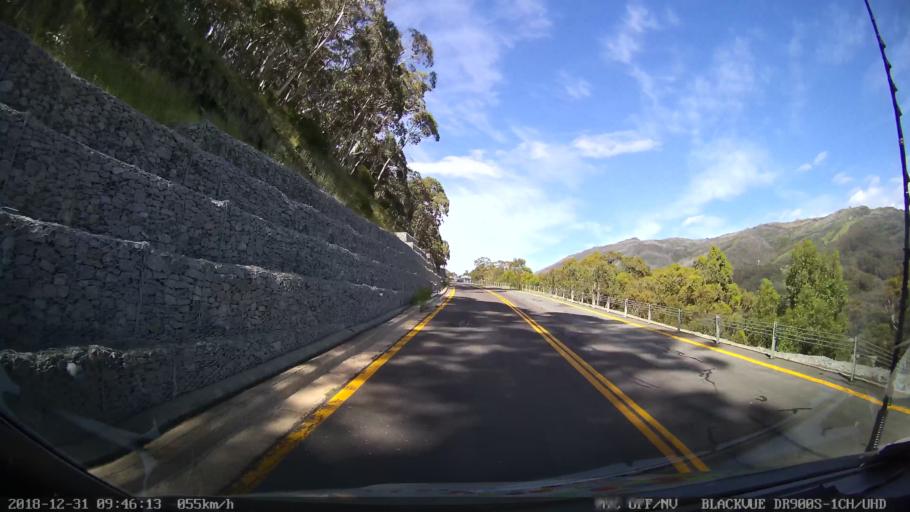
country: AU
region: New South Wales
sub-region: Snowy River
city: Jindabyne
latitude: -36.5030
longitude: 148.3110
